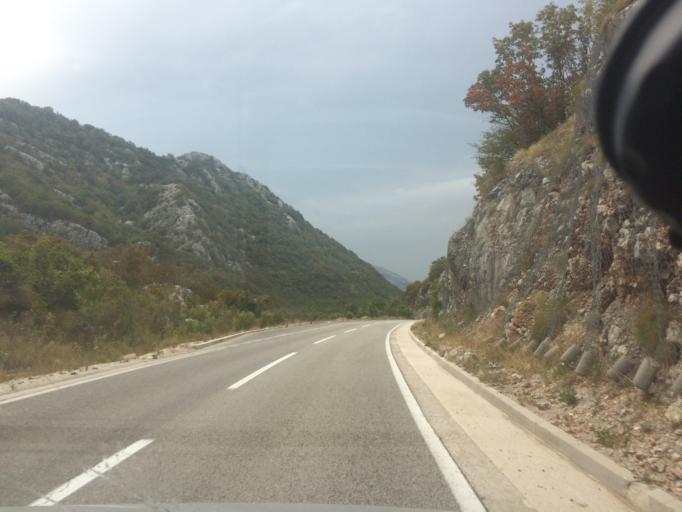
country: ME
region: Kotor
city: Risan
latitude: 42.5700
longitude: 18.6896
